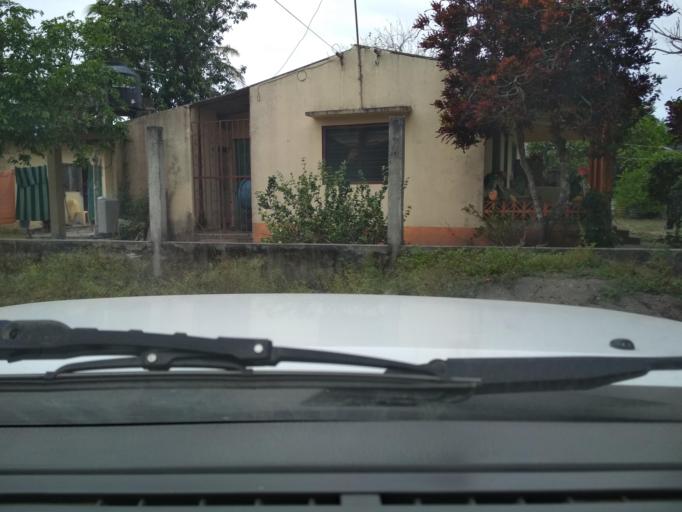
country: MX
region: Veracruz
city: Paso del Toro
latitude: 19.0557
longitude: -96.1338
